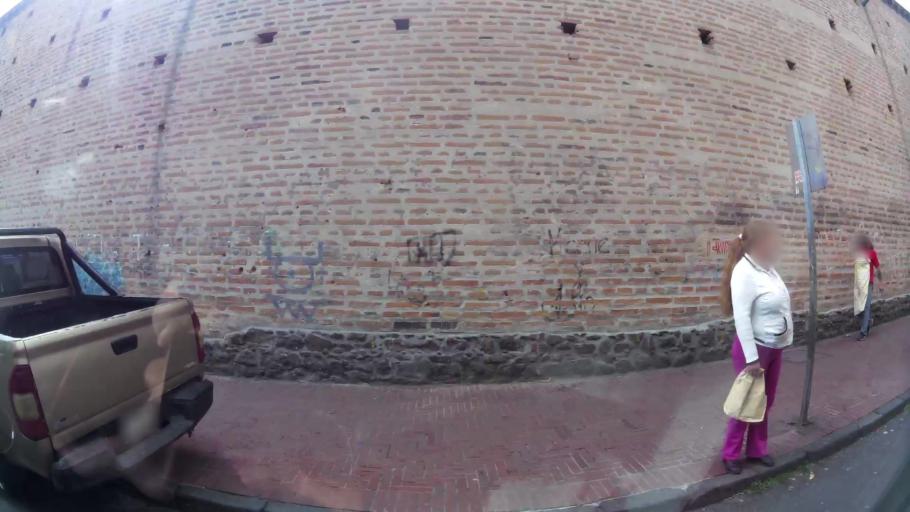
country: EC
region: Pichincha
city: Quito
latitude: -0.2191
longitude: -78.5162
